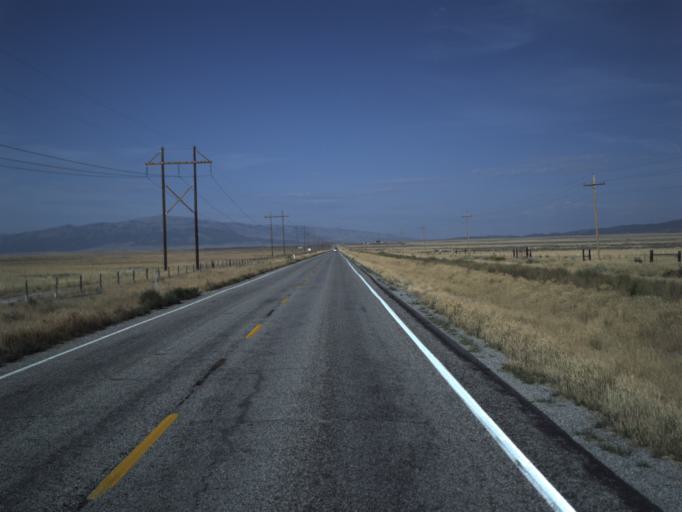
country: US
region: Idaho
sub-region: Oneida County
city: Malad City
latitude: 41.9663
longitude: -112.9482
